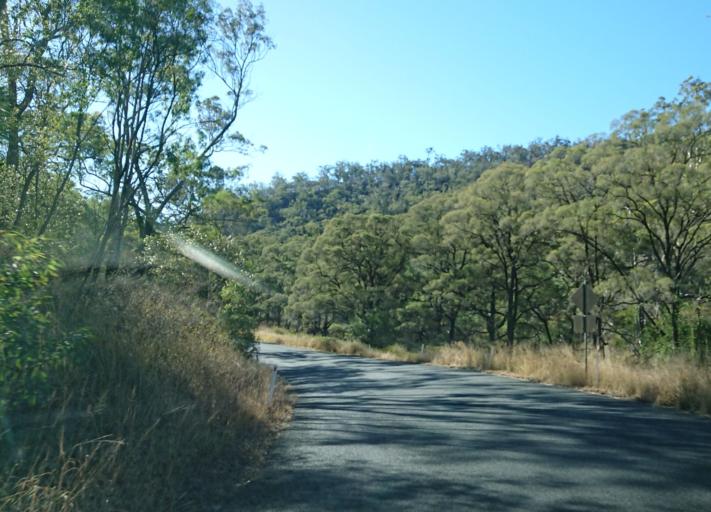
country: AU
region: Queensland
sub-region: Toowoomba
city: Top Camp
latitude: -27.7662
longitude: 152.0853
